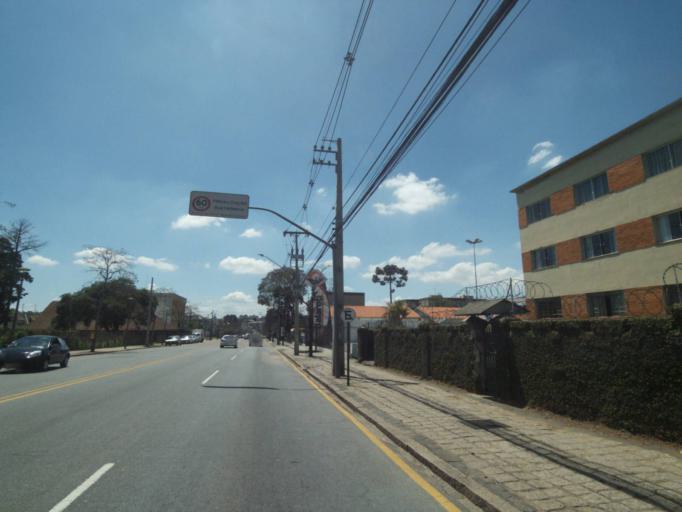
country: BR
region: Parana
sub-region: Curitiba
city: Curitiba
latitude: -25.3949
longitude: -49.2300
